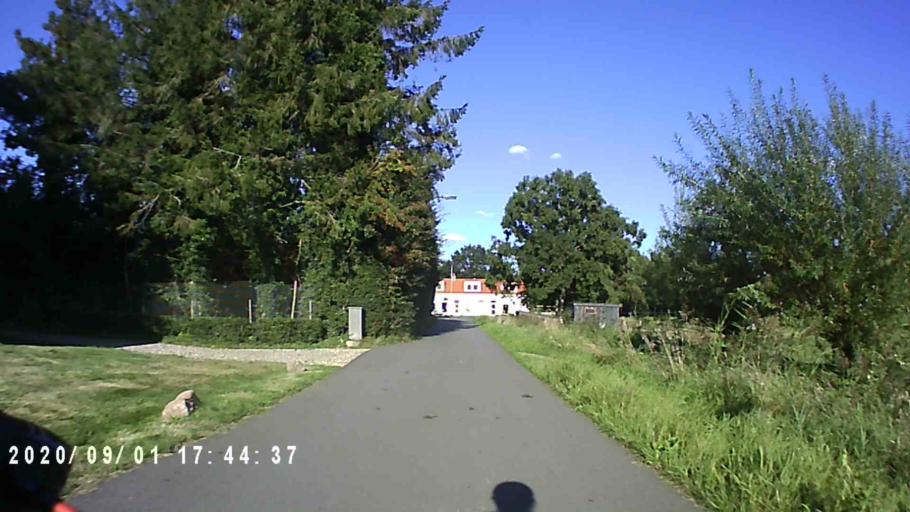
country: NL
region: Groningen
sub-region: Gemeente Hoogezand-Sappemeer
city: Hoogezand
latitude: 53.2168
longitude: 6.7380
